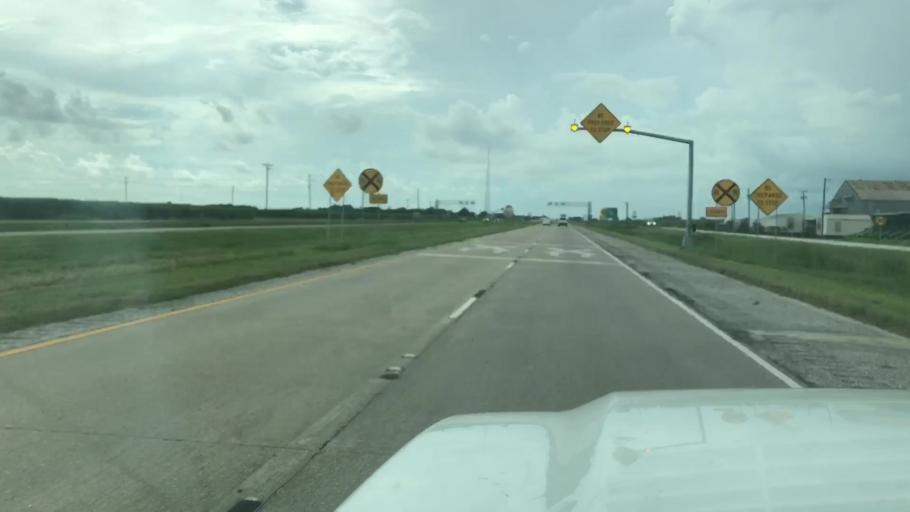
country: US
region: Louisiana
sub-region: Iberia Parish
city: Jeanerette
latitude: 29.9111
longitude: -91.7155
